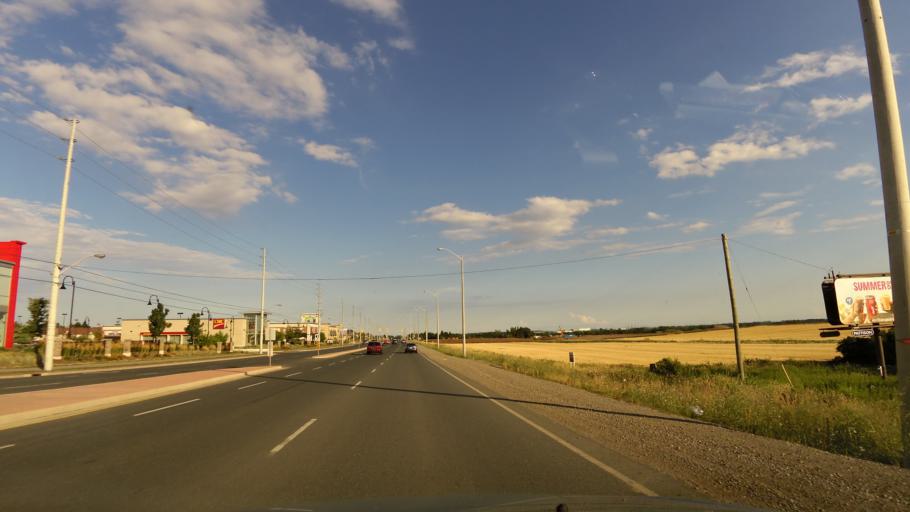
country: CA
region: Ontario
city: Brampton
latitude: 43.6571
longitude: -79.8165
